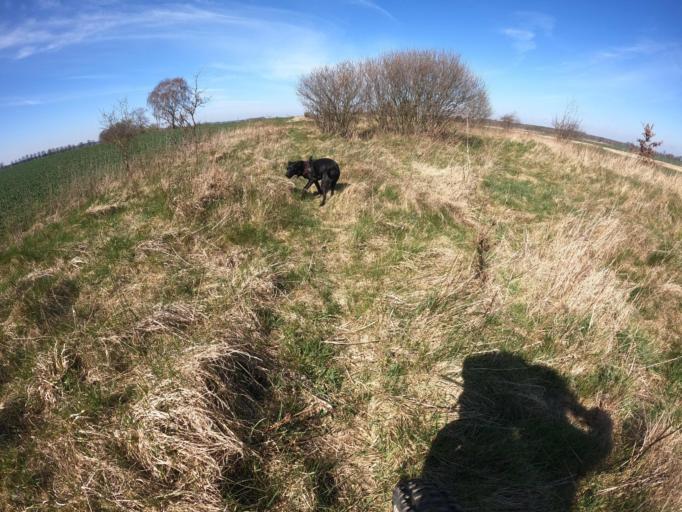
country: PL
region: West Pomeranian Voivodeship
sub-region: Powiat gryficki
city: Brojce
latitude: 53.9884
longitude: 15.3864
